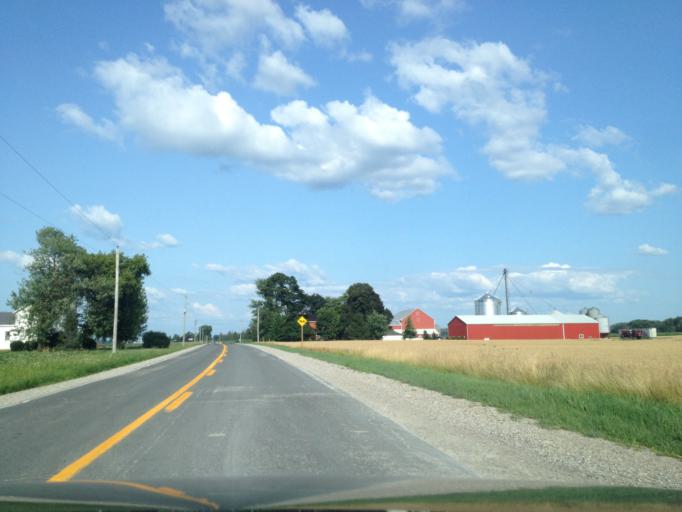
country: CA
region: Ontario
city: Ingersoll
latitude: 42.9677
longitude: -80.7315
